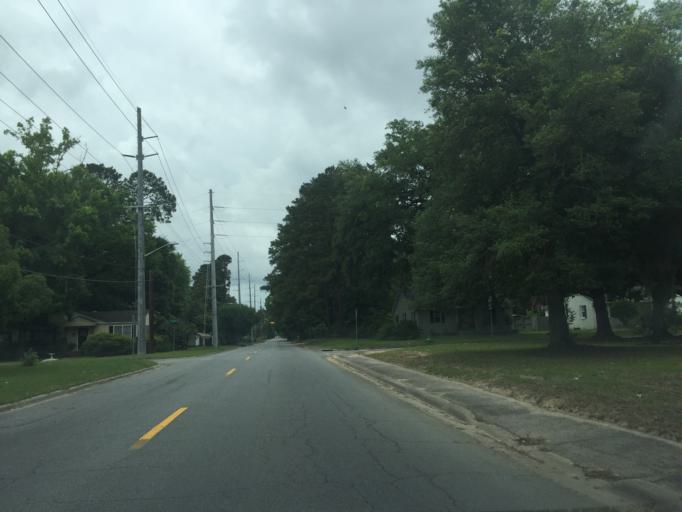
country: US
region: Georgia
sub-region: Chatham County
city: Thunderbolt
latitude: 32.0302
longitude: -81.1007
